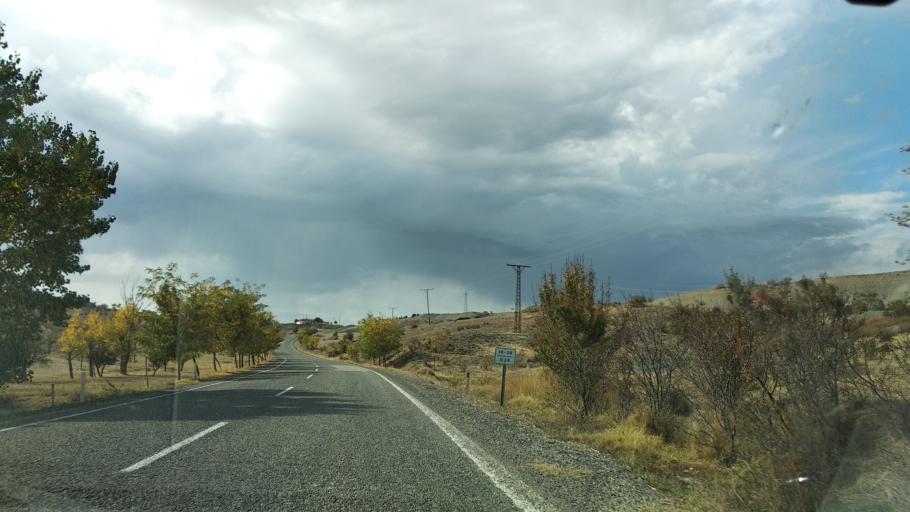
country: TR
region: Bolu
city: Seben
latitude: 40.3813
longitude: 31.5250
